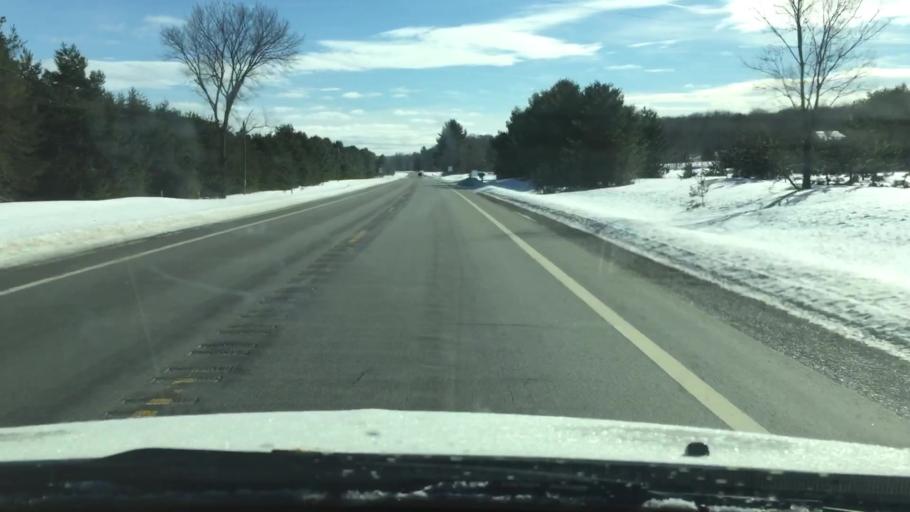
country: US
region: Michigan
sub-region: Charlevoix County
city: East Jordan
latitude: 45.0751
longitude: -85.0873
